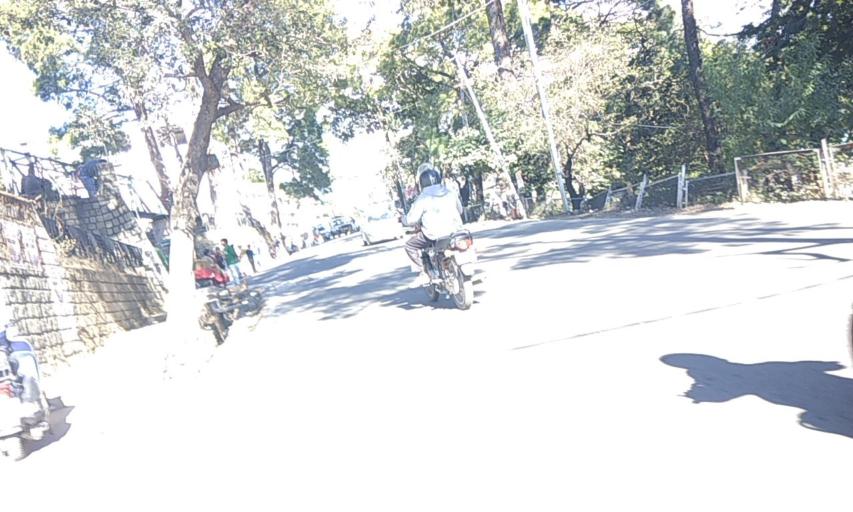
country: IN
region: Himachal Pradesh
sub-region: Kangra
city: Dharmsala
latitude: 32.2153
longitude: 76.3173
